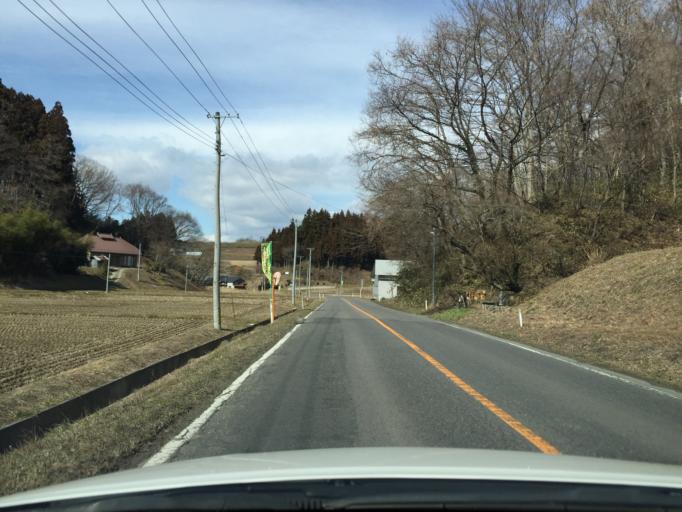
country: JP
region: Fukushima
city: Funehikimachi-funehiki
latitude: 37.4089
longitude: 140.5469
